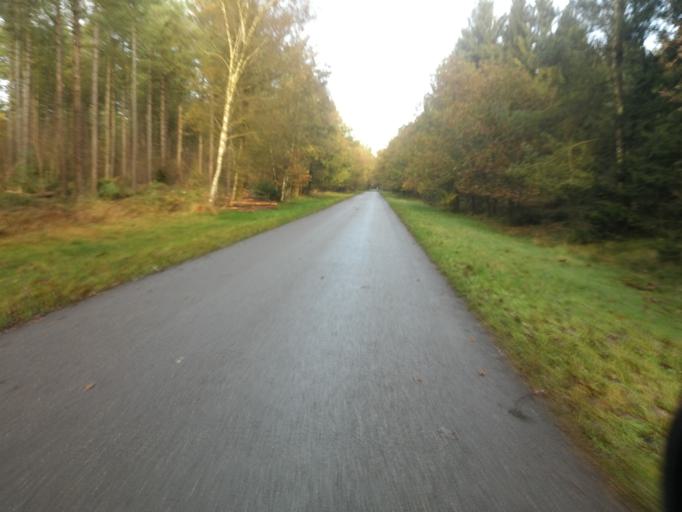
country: NL
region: Utrecht
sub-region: Gemeente Utrechtse Heuvelrug
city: Maarn
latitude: 52.1001
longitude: 5.3776
